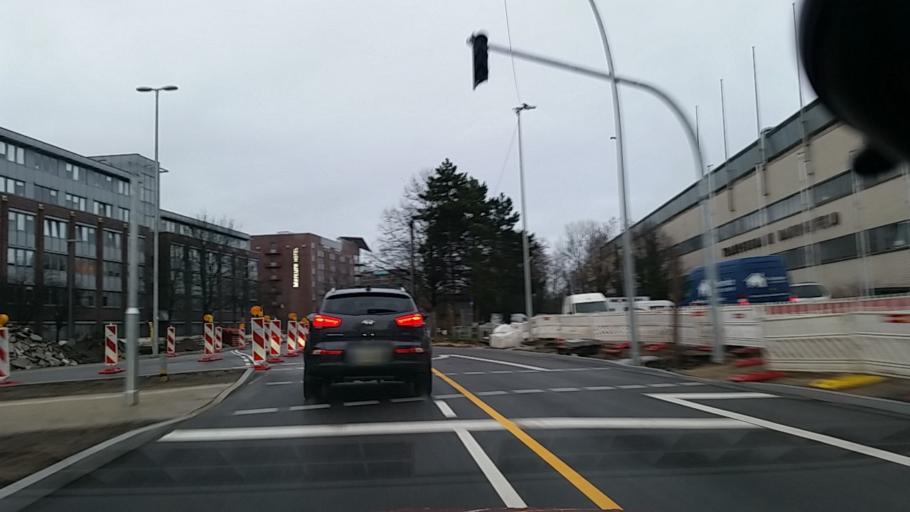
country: DE
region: Hamburg
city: Eidelstedt
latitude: 53.5743
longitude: 9.8920
